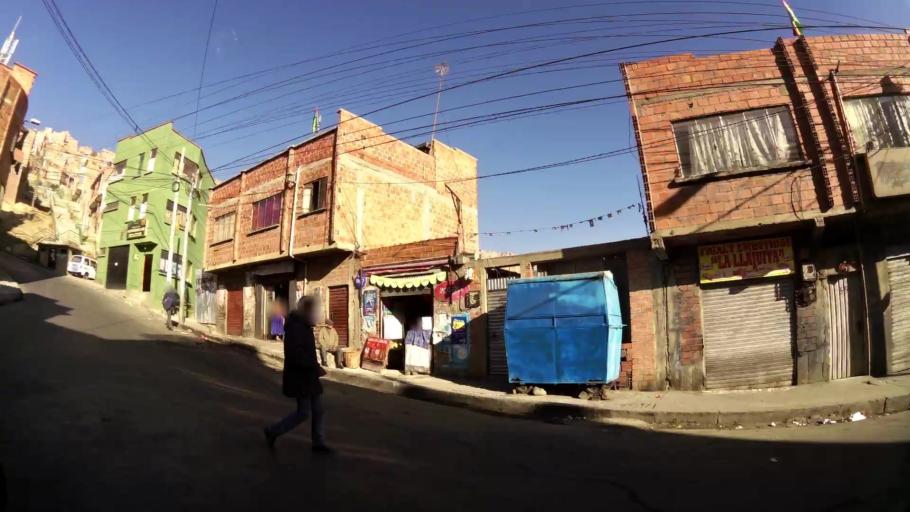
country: BO
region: La Paz
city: La Paz
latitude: -16.5047
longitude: -68.1531
